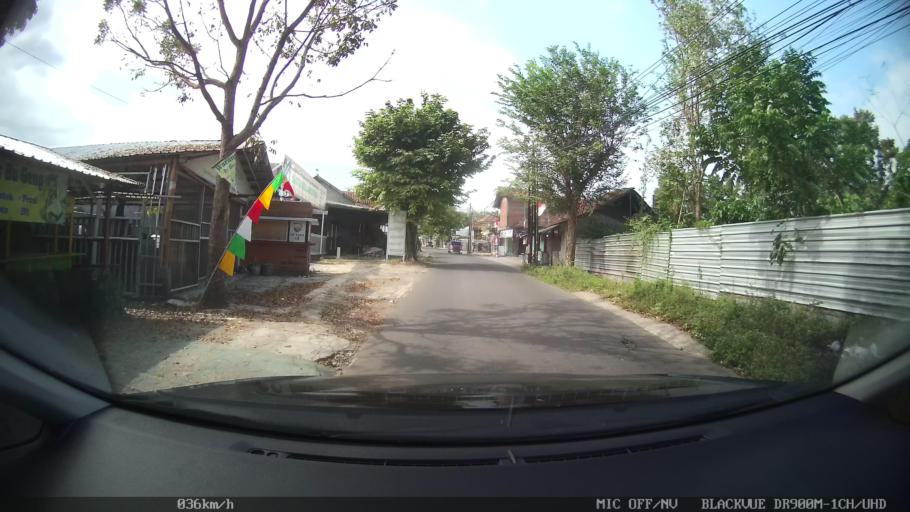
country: ID
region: Daerah Istimewa Yogyakarta
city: Depok
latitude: -7.7410
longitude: 110.4199
